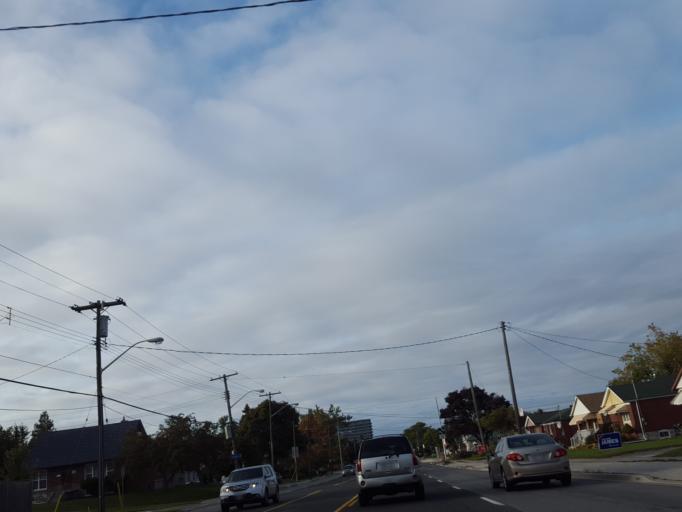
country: CA
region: Ontario
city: Scarborough
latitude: 43.7393
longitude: -79.2922
